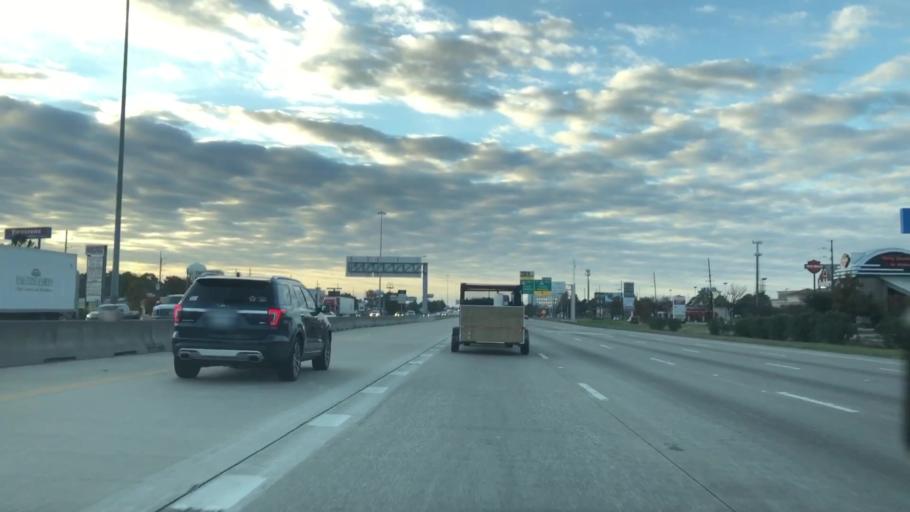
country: US
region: Texas
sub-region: Montgomery County
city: Oak Ridge North
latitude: 30.1344
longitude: -95.4447
